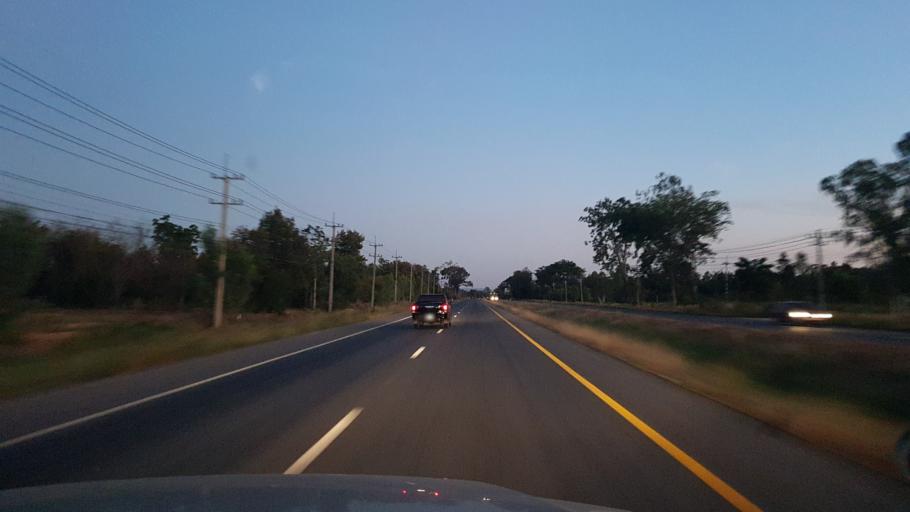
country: TH
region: Chaiyaphum
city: Phu Khiao
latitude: 16.3108
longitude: 102.2018
